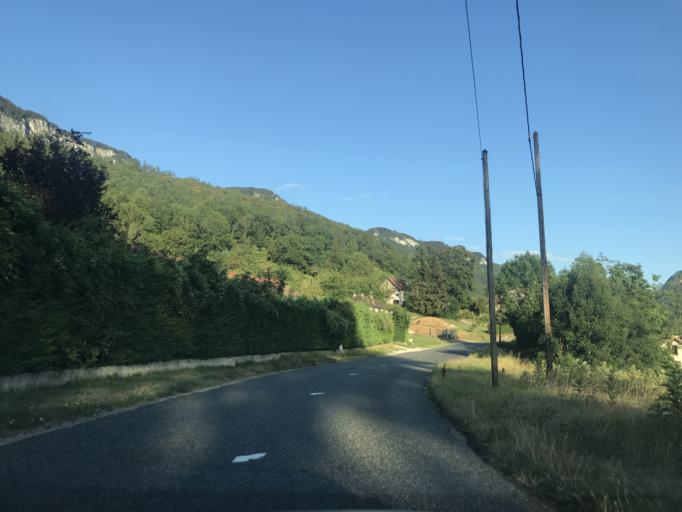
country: FR
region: Rhone-Alpes
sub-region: Departement de la Savoie
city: Yenne
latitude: 45.7178
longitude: 5.8179
